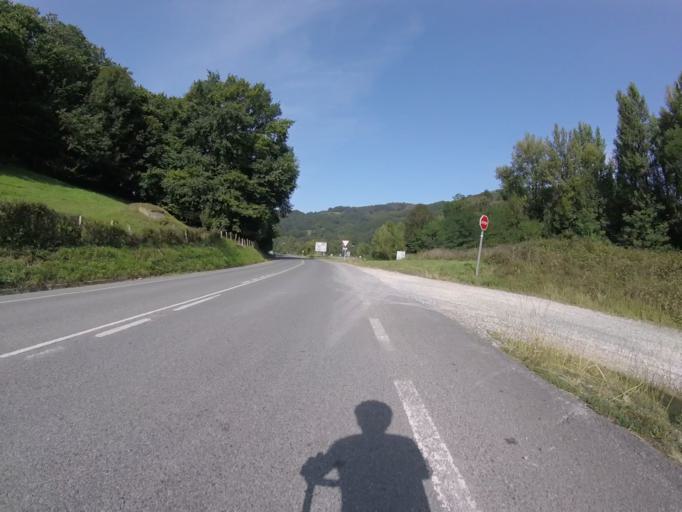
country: ES
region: Navarre
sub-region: Provincia de Navarra
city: Doneztebe
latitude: 43.1401
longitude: -1.5603
